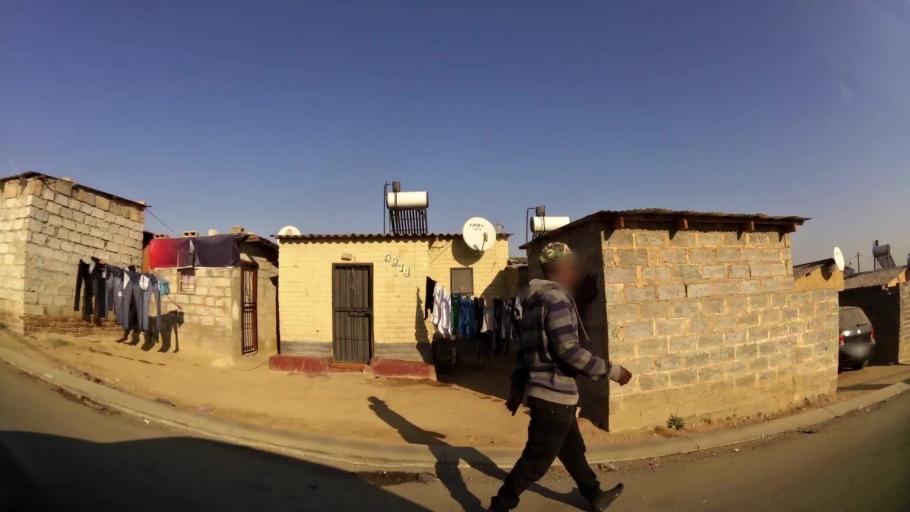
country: ZA
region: Gauteng
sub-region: City of Johannesburg Metropolitan Municipality
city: Modderfontein
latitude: -26.0860
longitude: 28.1141
